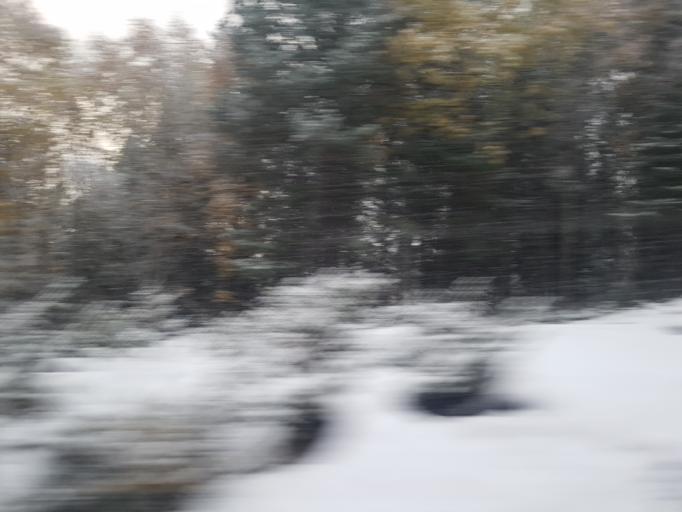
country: NO
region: Oppland
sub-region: Dovre
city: Dombas
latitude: 62.0783
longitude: 9.1262
